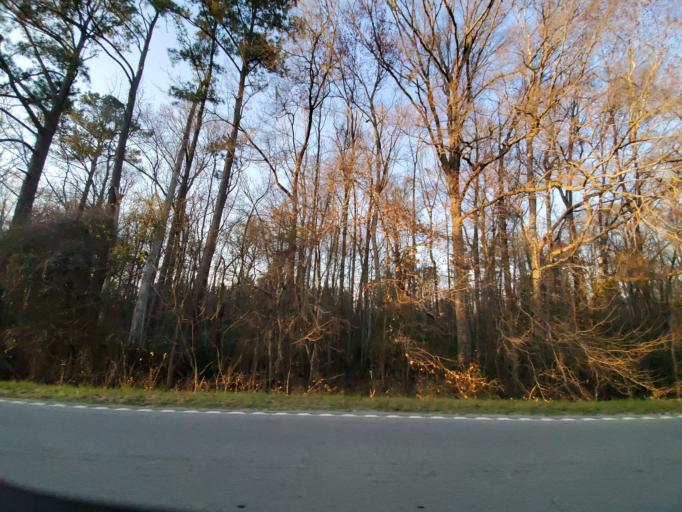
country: US
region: South Carolina
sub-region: Dorchester County
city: Saint George
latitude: 33.0521
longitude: -80.4842
